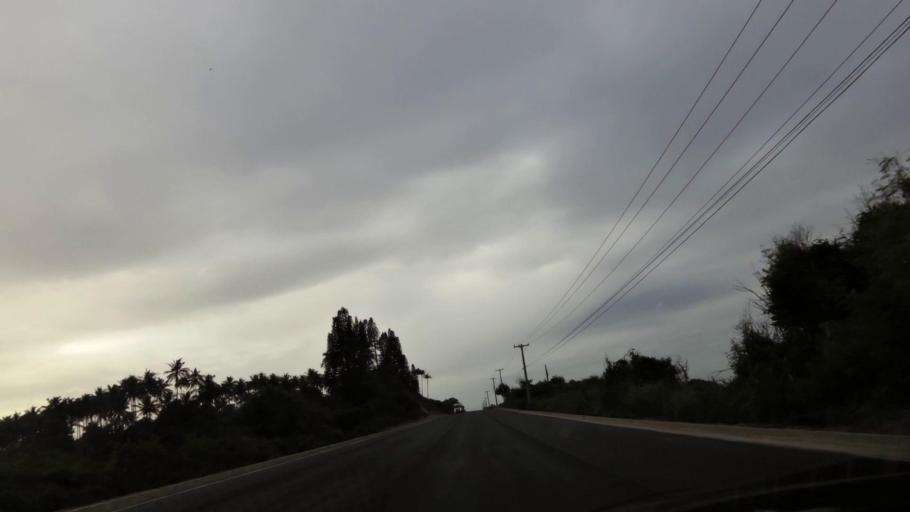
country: BR
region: Espirito Santo
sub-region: Guarapari
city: Guarapari
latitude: -20.7640
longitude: -40.5706
